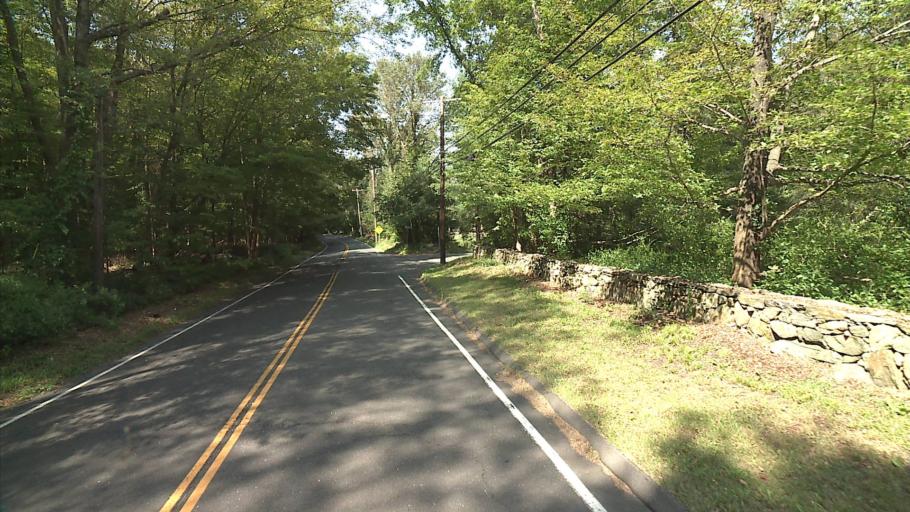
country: US
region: Connecticut
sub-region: Fairfield County
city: Georgetown
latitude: 41.2663
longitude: -73.3294
